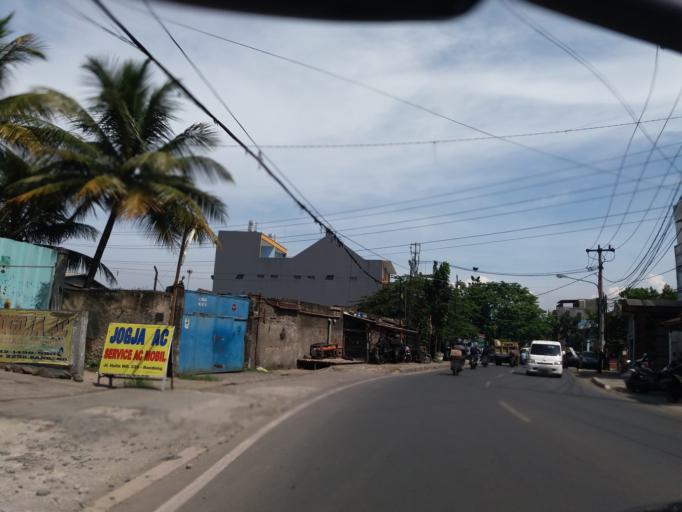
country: ID
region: West Java
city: Margahayukencana
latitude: -6.9356
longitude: 107.5711
